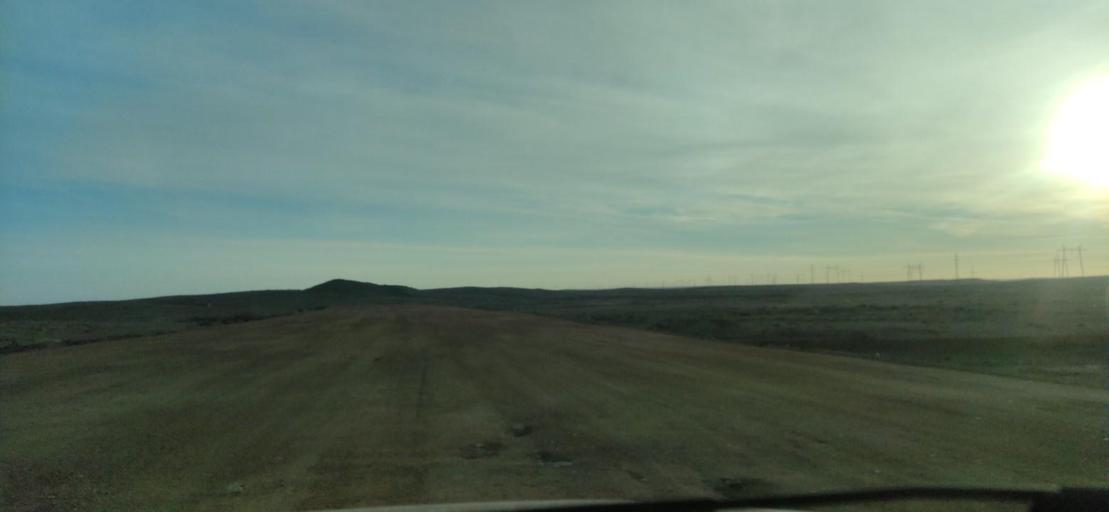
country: KZ
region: Qaraghandy
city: Saryshaghan
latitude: 46.1198
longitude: 73.5949
